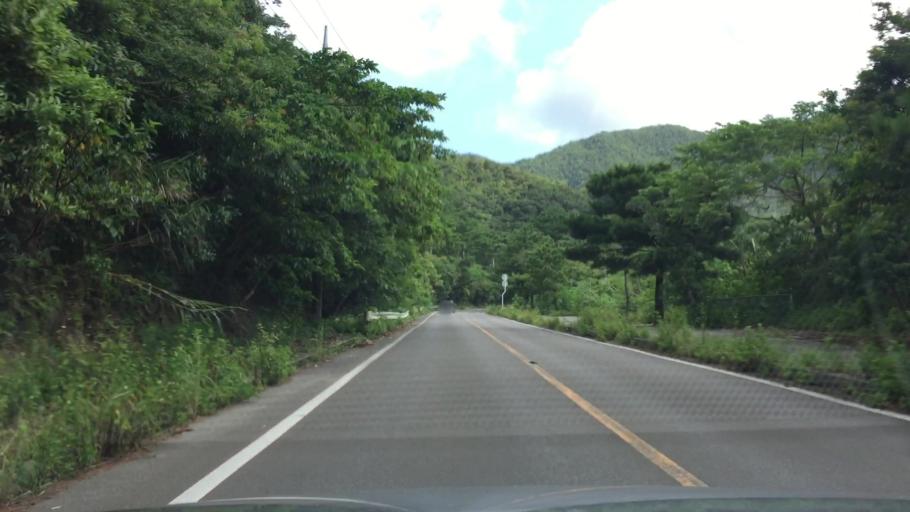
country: JP
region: Okinawa
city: Ishigaki
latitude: 24.4305
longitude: 124.2104
